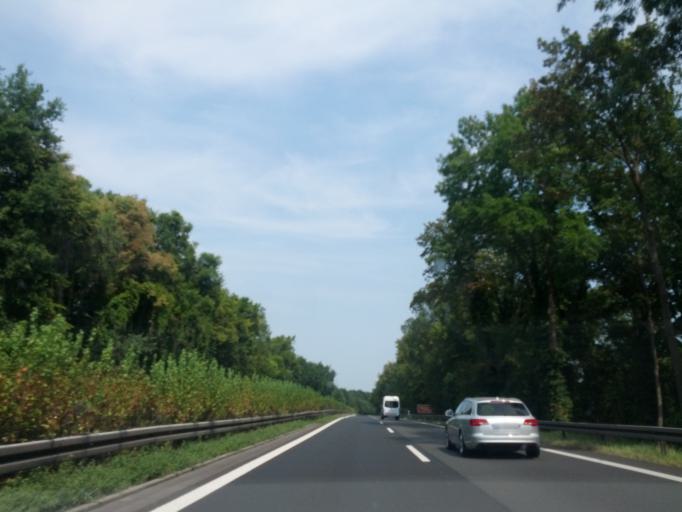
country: DE
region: Brandenburg
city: Werder
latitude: 52.4027
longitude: 12.8703
